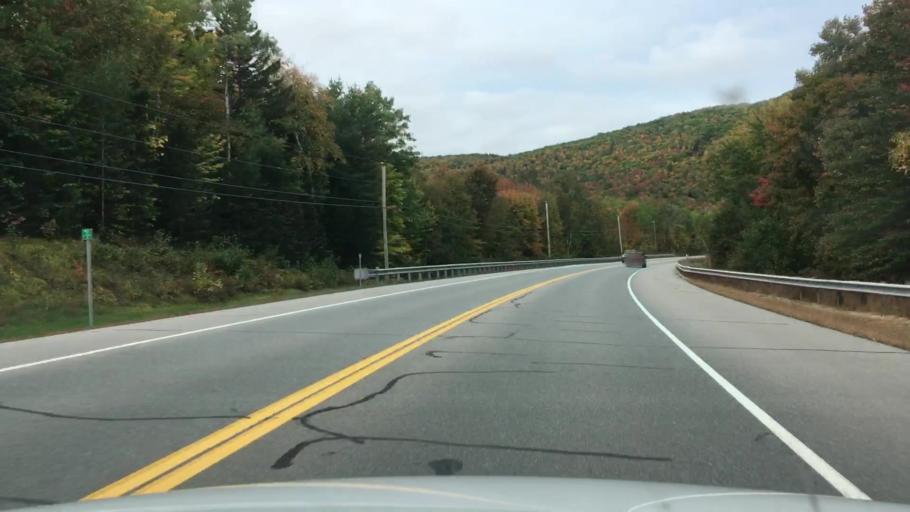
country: US
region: New Hampshire
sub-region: Coos County
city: Gorham
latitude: 44.3967
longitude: -71.0685
